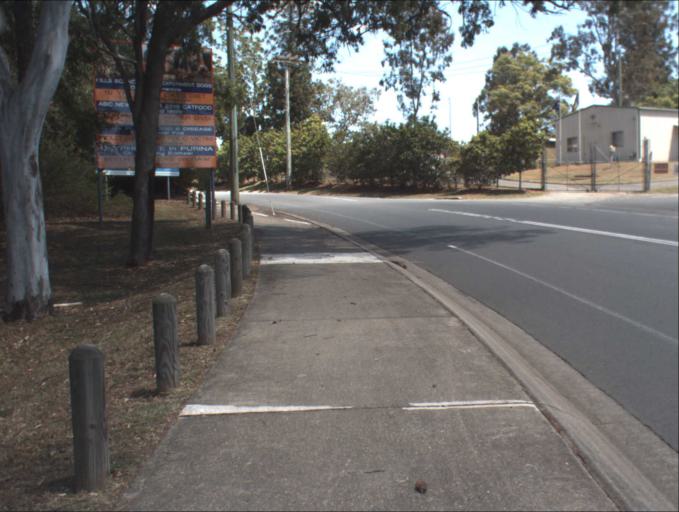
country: AU
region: Queensland
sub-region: Gold Coast
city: Yatala
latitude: -27.7255
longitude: 153.2188
